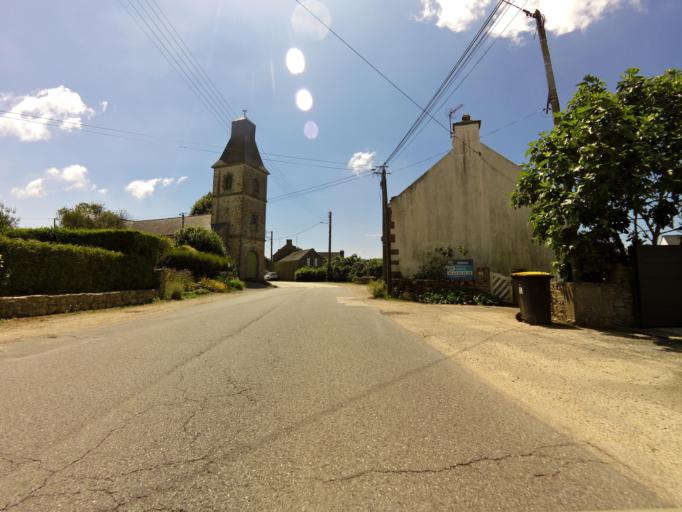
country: FR
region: Brittany
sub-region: Departement du Morbihan
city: Theix
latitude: 47.6114
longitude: -2.6829
